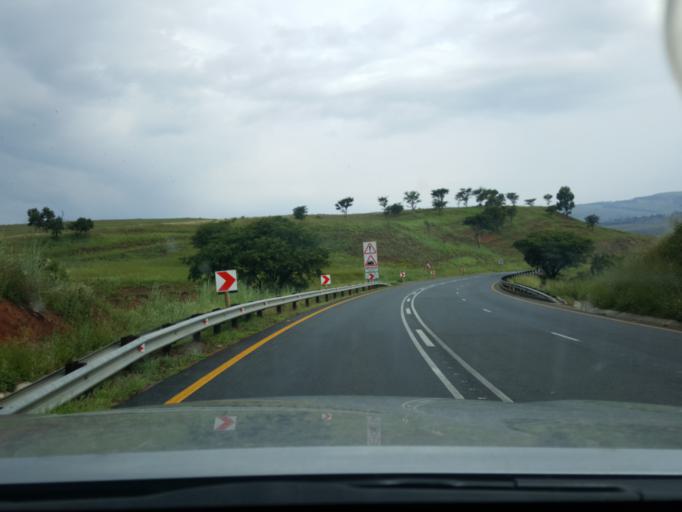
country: ZA
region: Mpumalanga
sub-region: Nkangala District Municipality
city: Belfast
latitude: -25.6273
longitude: 30.3394
